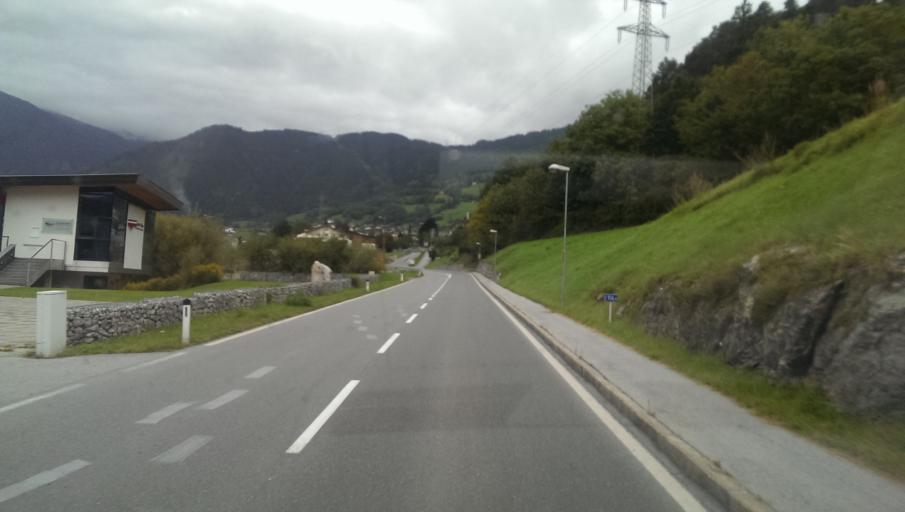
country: AT
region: Tyrol
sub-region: Politischer Bezirk Landeck
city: Grins
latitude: 47.1361
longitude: 10.5215
